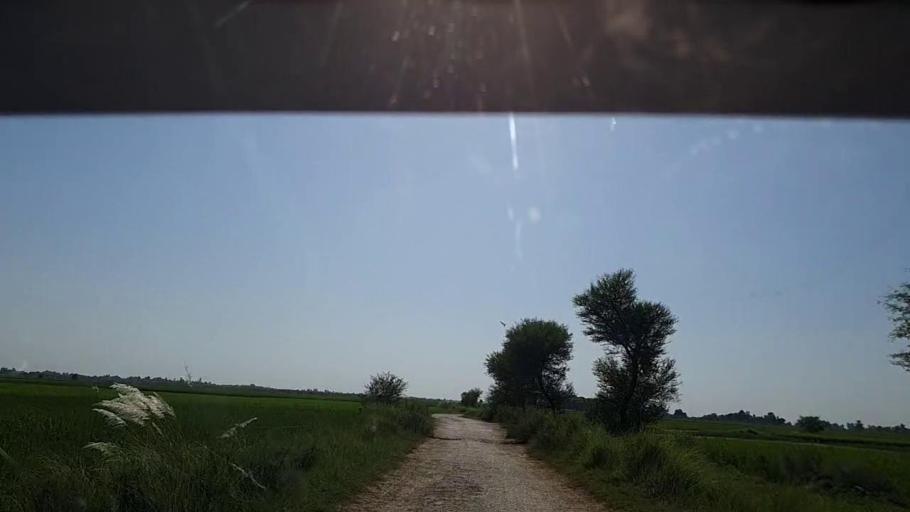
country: PK
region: Sindh
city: Ghauspur
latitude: 28.1786
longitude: 69.0363
